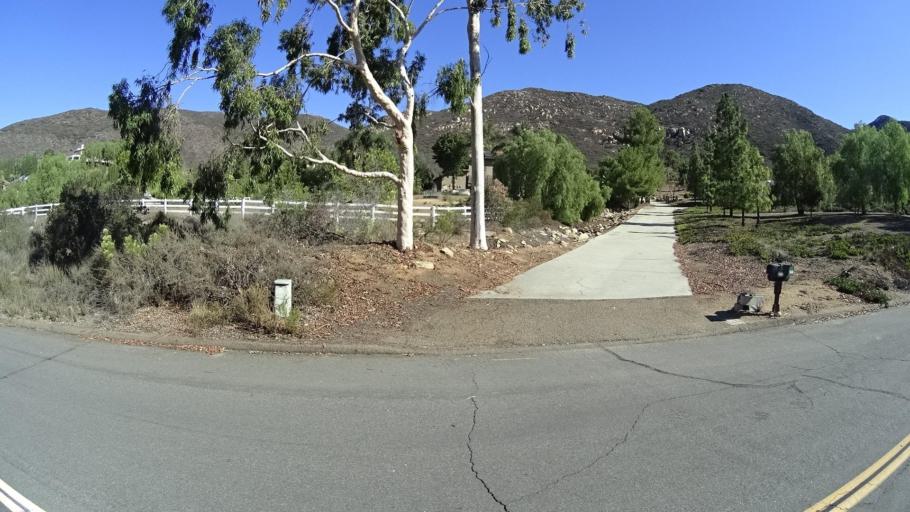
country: US
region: California
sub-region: San Diego County
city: Jamul
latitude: 32.7410
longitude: -116.8558
